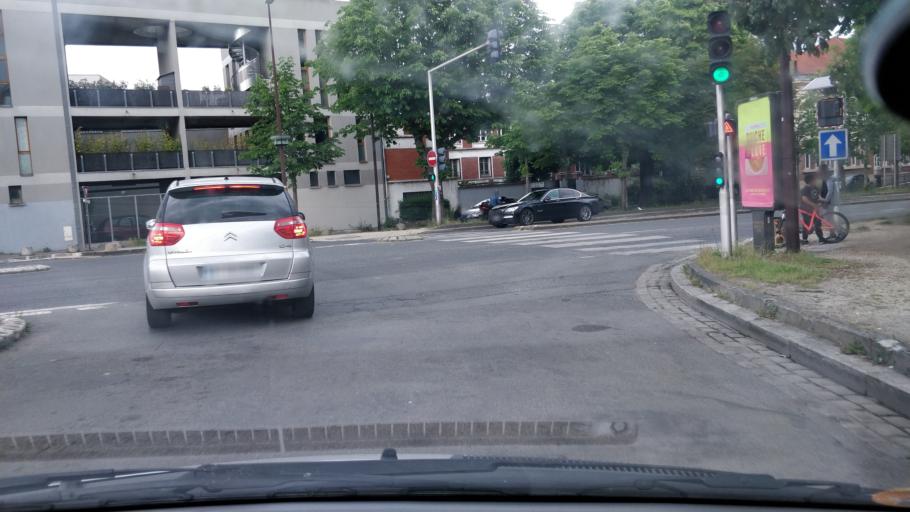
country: FR
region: Ile-de-France
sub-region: Departement de Seine-Saint-Denis
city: Montreuil
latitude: 48.8691
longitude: 2.4326
